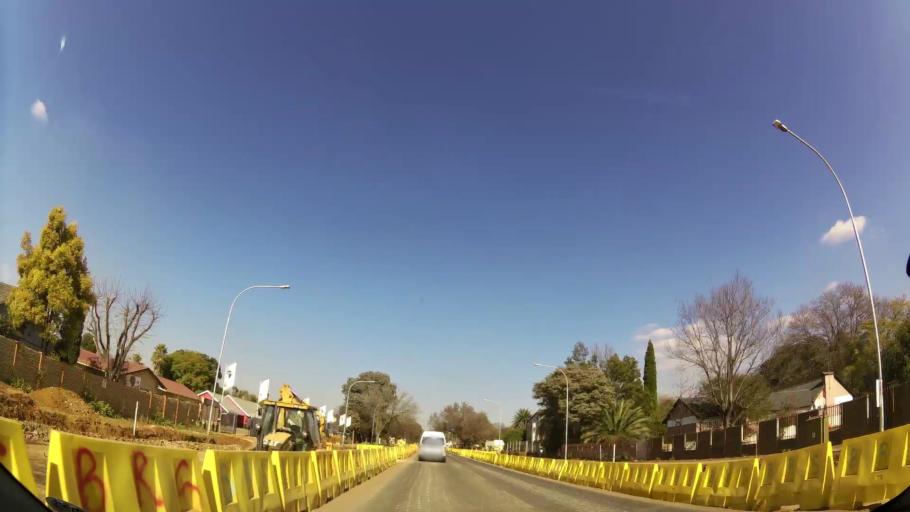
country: ZA
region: Gauteng
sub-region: Ekurhuleni Metropolitan Municipality
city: Benoni
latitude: -26.1489
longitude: 28.3402
